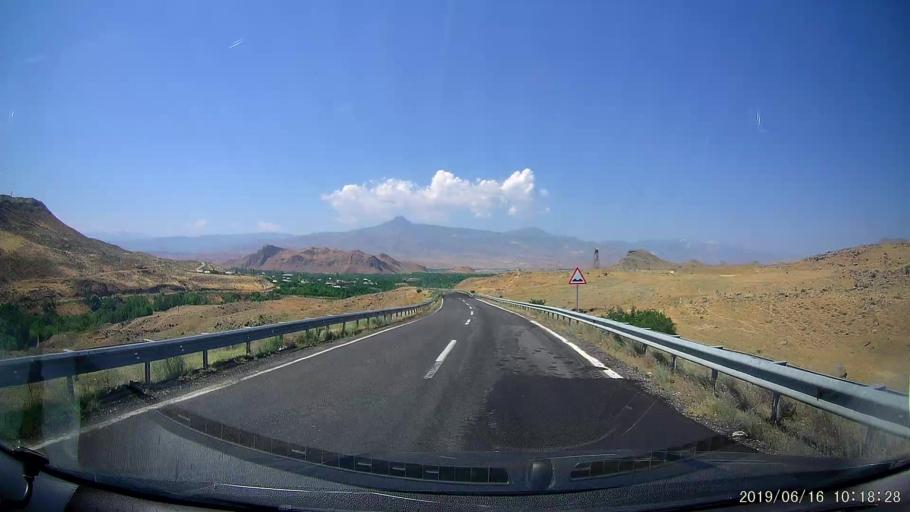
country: TR
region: Igdir
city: Tuzluca
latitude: 40.1602
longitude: 43.6677
